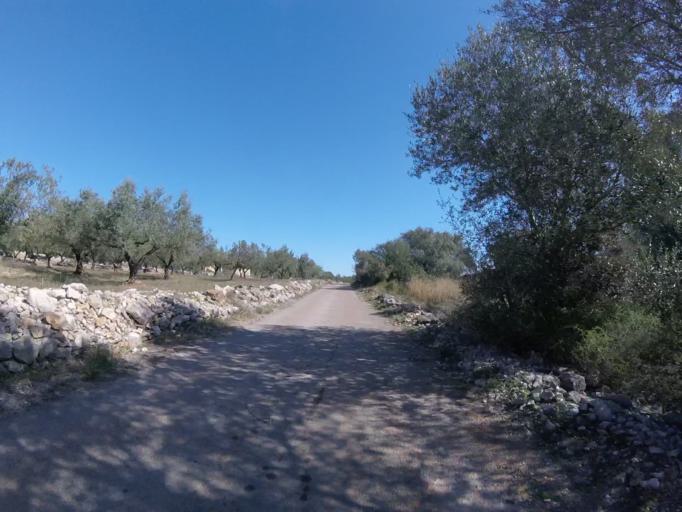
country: ES
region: Valencia
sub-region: Provincia de Castello
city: Santa Magdalena de Pulpis
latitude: 40.3552
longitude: 0.2836
